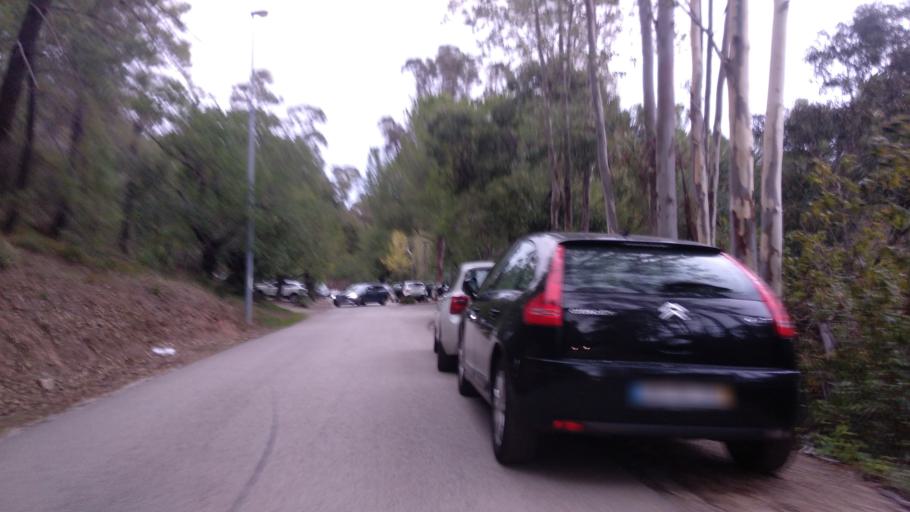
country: PT
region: Faro
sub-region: Sao Bras de Alportel
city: Sao Bras de Alportel
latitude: 37.1842
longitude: -7.9139
